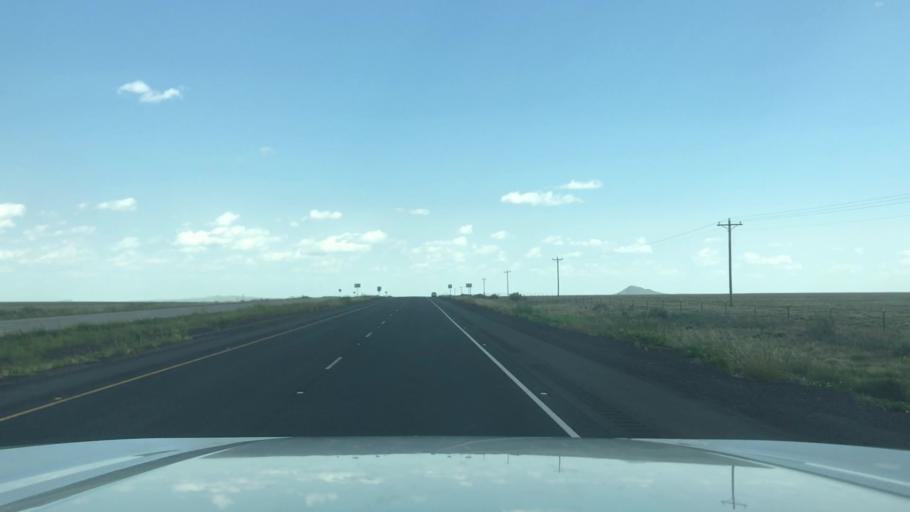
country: US
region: New Mexico
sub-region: Union County
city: Clayton
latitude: 36.6339
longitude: -103.7185
